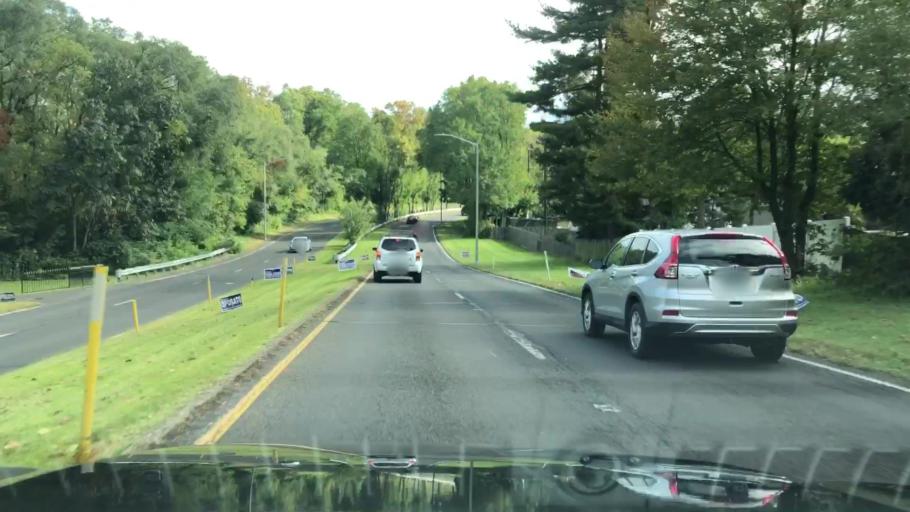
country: US
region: Pennsylvania
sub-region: Bucks County
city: Levittown
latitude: 40.1629
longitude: -74.8354
